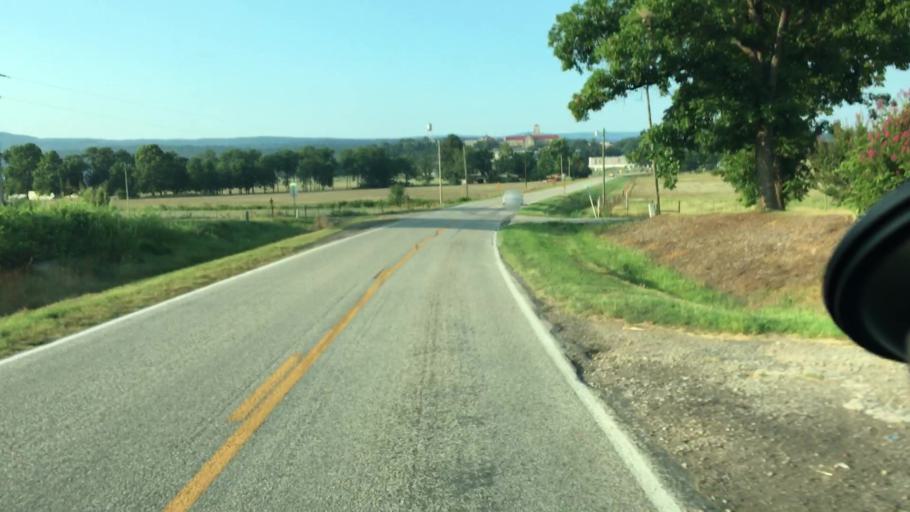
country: US
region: Arkansas
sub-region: Logan County
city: Paris
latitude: 35.3089
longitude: -93.6326
